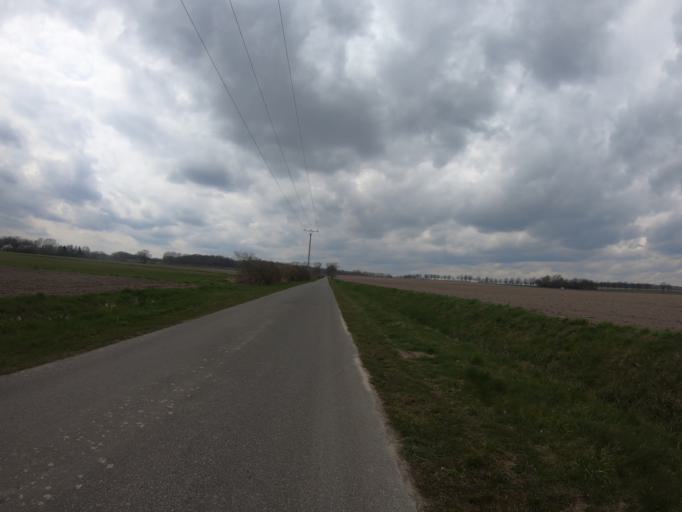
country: DE
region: Lower Saxony
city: Hankensbuttel
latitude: 52.7280
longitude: 10.6426
